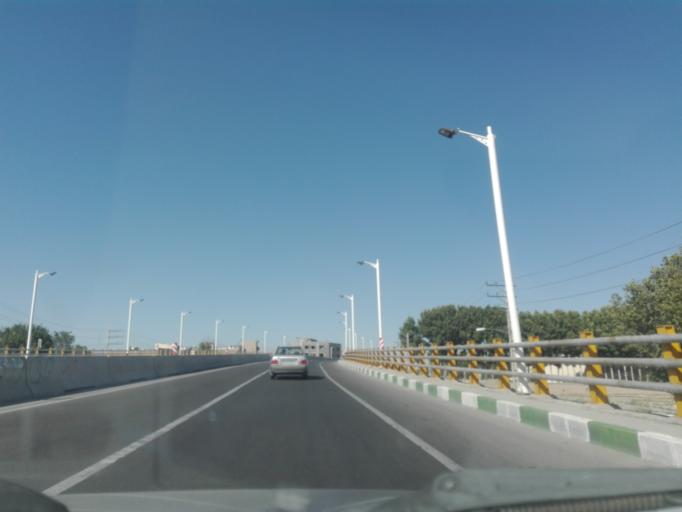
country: IR
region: Tehran
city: Shahriar
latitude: 35.6357
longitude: 51.0632
